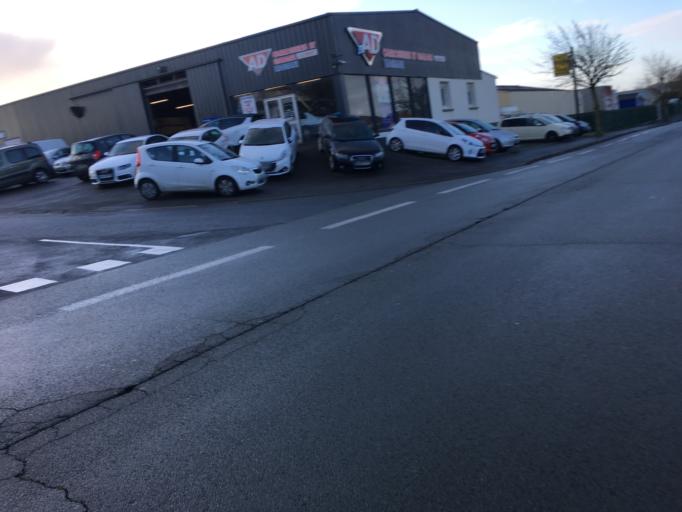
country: FR
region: Poitou-Charentes
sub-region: Departement de la Charente-Maritime
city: Nieul-sur-Mer
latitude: 46.2028
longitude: -1.1716
